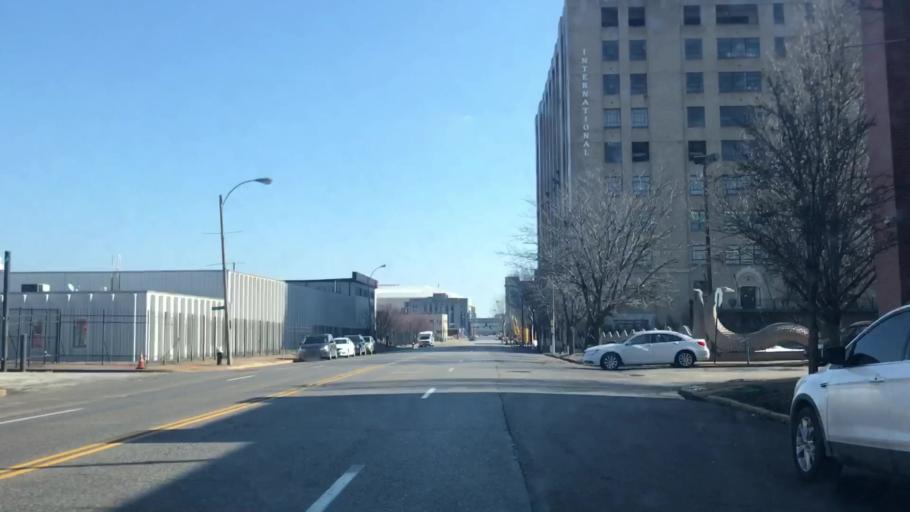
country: US
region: Missouri
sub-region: City of Saint Louis
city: St. Louis
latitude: 38.6344
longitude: -90.2016
